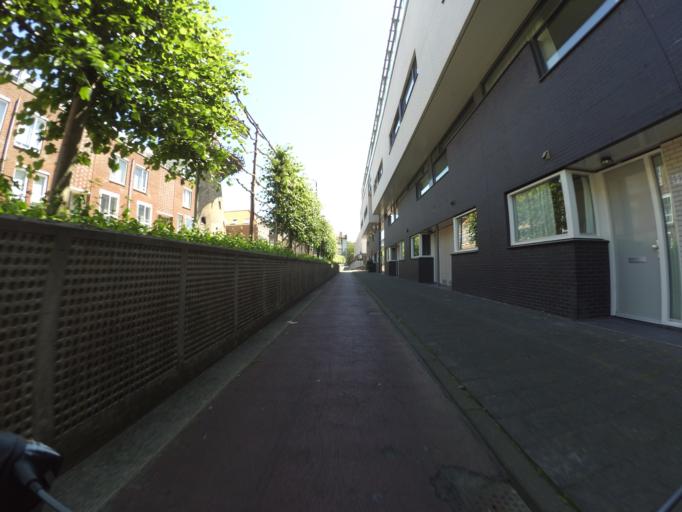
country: NL
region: South Holland
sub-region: Gemeente Dordrecht
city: Dordrecht
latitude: 51.8157
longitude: 4.6782
